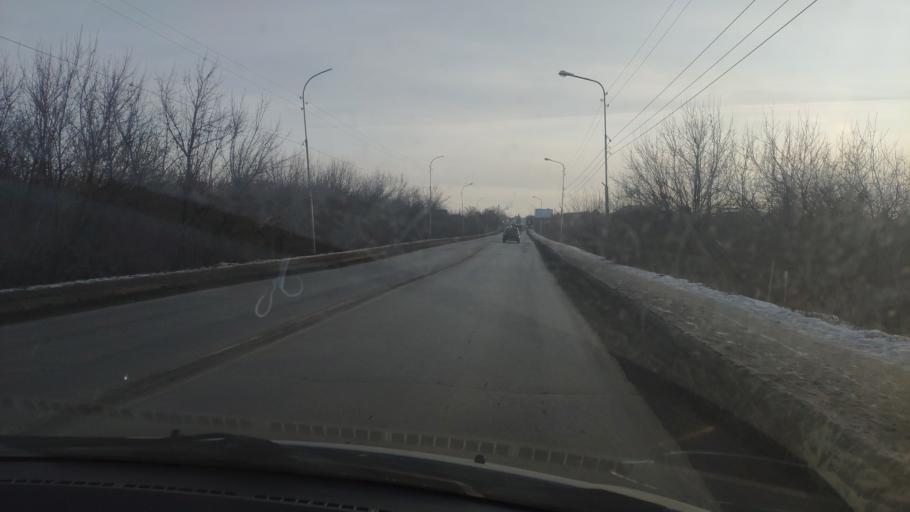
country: RU
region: Kurgan
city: Shadrinsk
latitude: 56.0736
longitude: 63.6428
